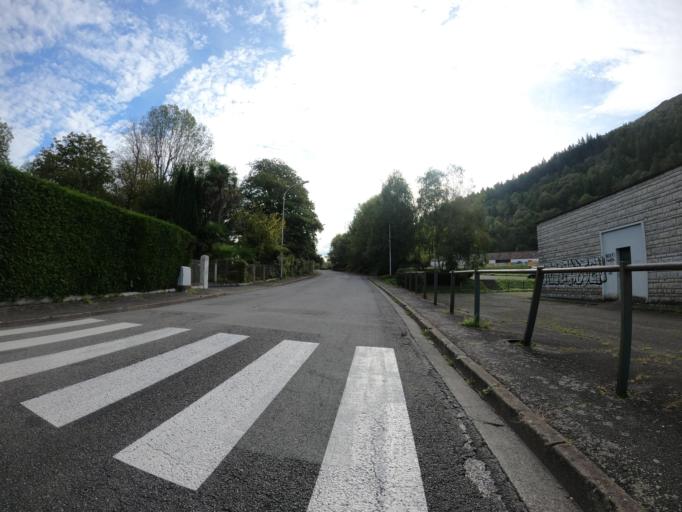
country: FR
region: Midi-Pyrenees
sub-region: Departement des Hautes-Pyrenees
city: Lourdes
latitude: 43.0954
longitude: -0.0342
